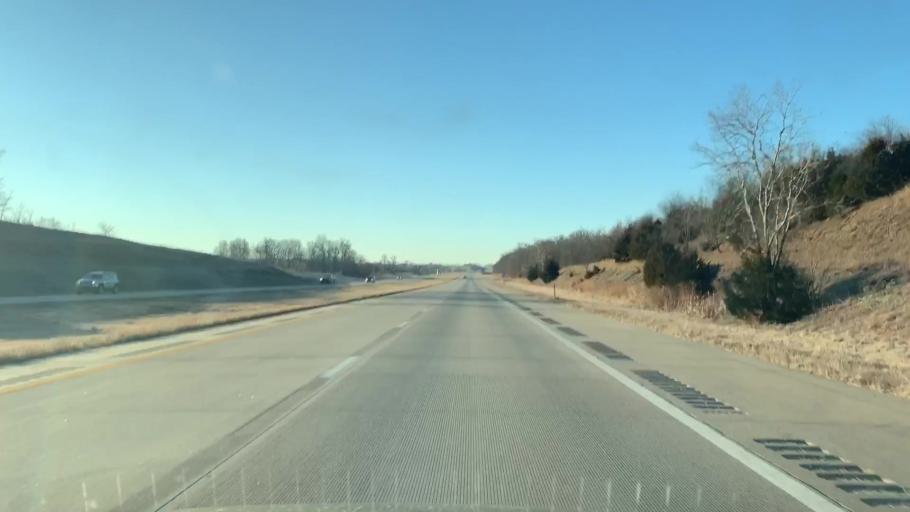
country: US
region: Kansas
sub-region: Linn County
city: Pleasanton
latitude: 38.0212
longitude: -94.7039
